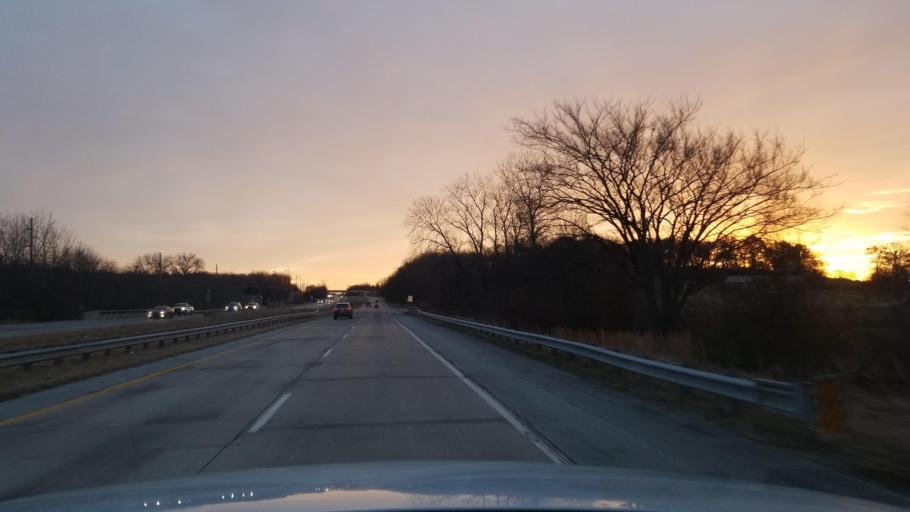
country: US
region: Indiana
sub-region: Posey County
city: Mount Vernon
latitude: 37.9417
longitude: -87.7482
